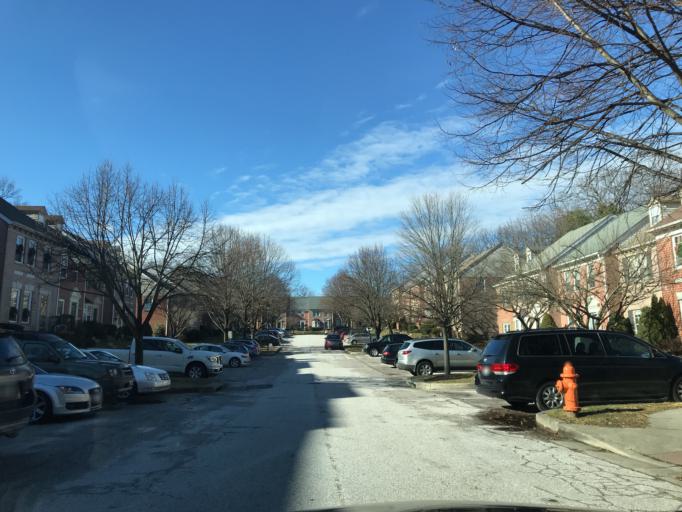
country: US
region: Maryland
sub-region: Baltimore County
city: Carney
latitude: 39.4089
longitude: -76.5474
